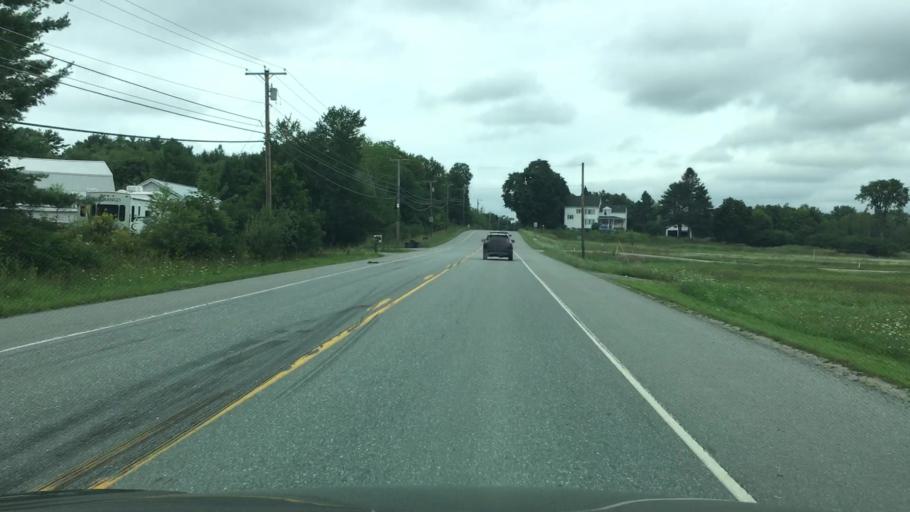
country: US
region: Maine
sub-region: Penobscot County
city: Orrington
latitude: 44.7094
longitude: -68.8250
